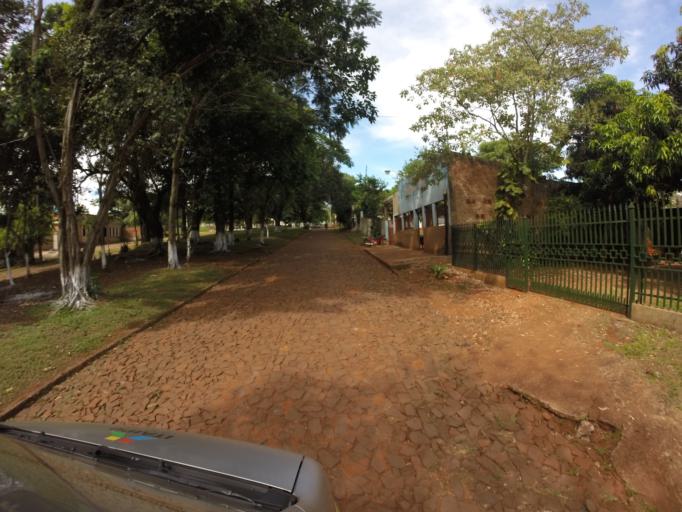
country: PY
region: Alto Parana
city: Ciudad del Este
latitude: -25.4402
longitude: -54.6440
